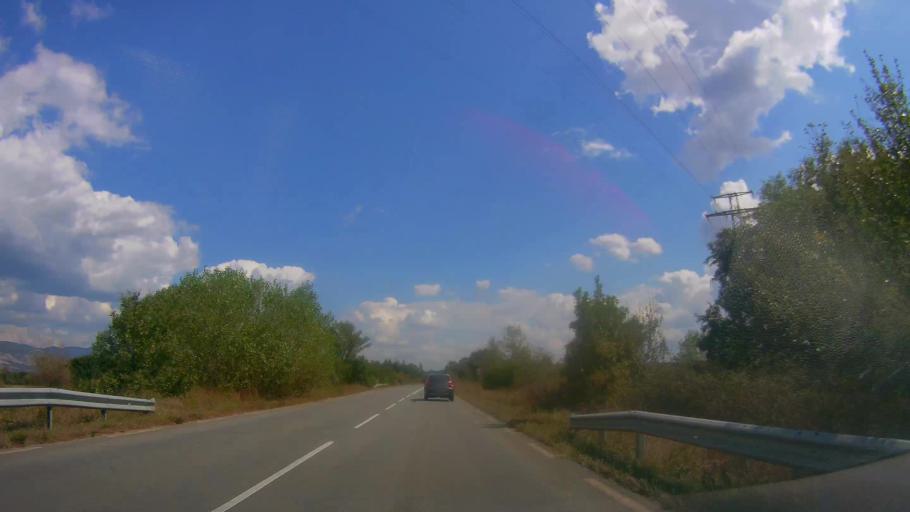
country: BG
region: Sliven
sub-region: Obshtina Tvurditsa
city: Tvurditsa
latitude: 42.6528
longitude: 25.9678
